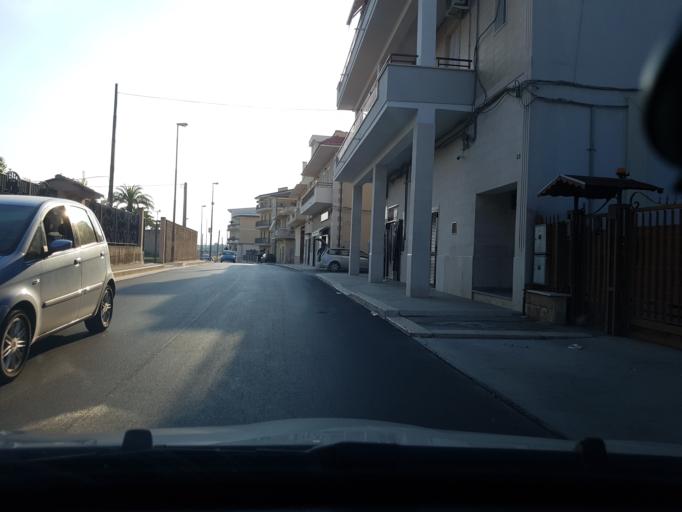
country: IT
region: Apulia
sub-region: Provincia di Foggia
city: Cerignola
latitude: 41.2654
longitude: 15.8850
